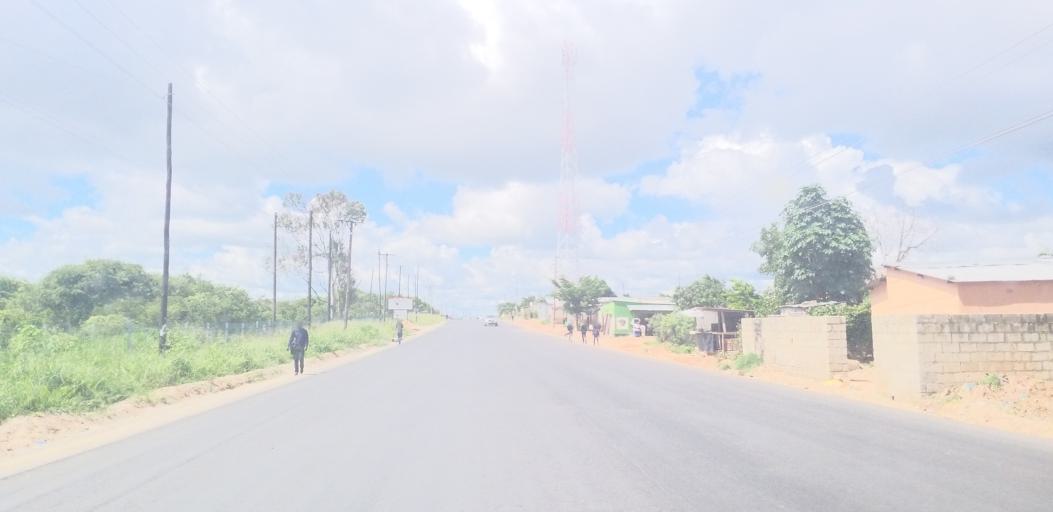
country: ZM
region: Lusaka
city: Lusaka
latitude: -15.3610
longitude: 28.3219
